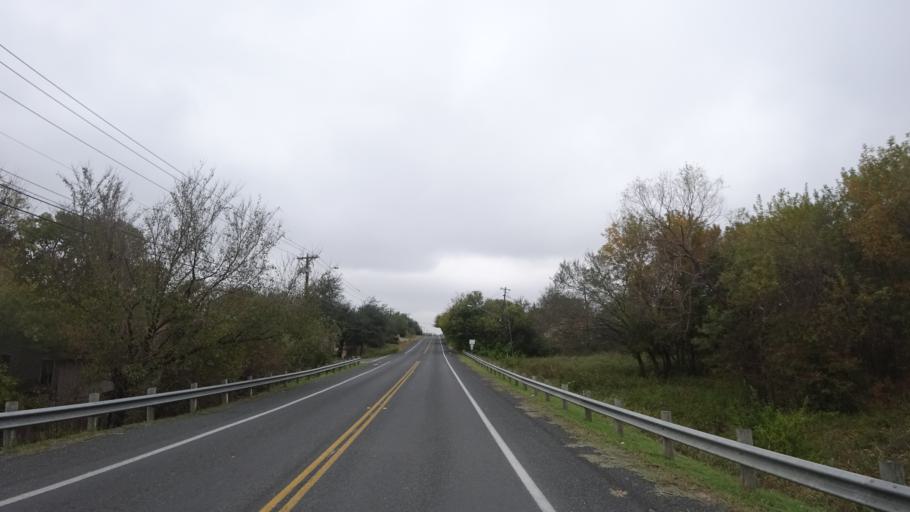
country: US
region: Texas
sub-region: Travis County
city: Pflugerville
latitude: 30.3885
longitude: -97.6544
